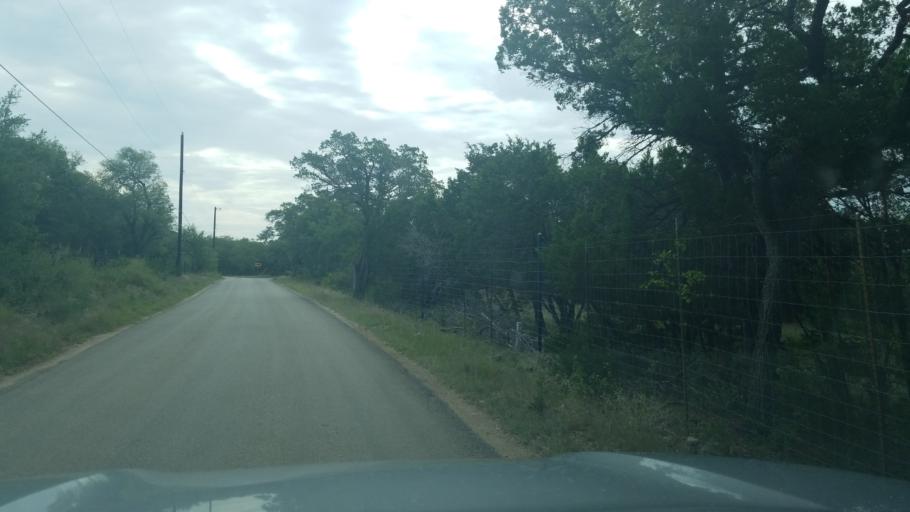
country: US
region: Texas
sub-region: Comal County
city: Bulverde
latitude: 29.7650
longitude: -98.4103
